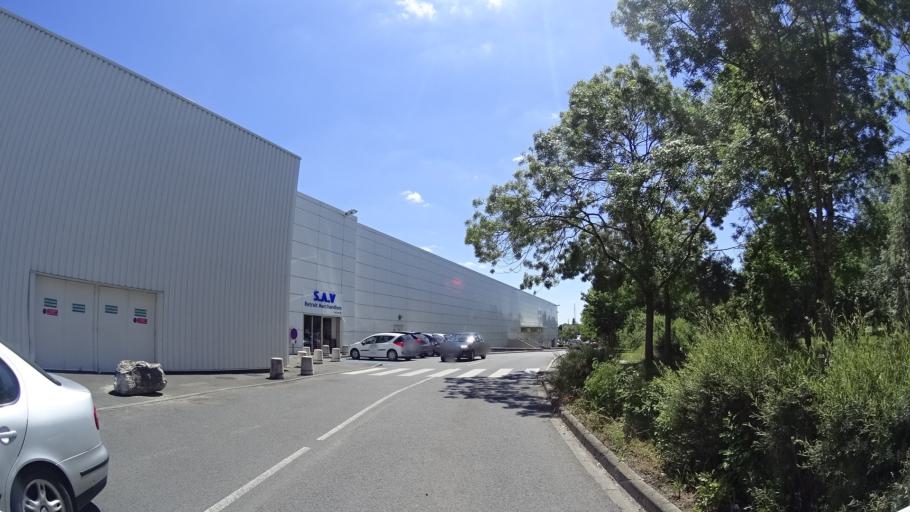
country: FR
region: Pays de la Loire
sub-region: Departement de Maine-et-Loire
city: Saumur
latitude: 47.2621
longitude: -0.0921
